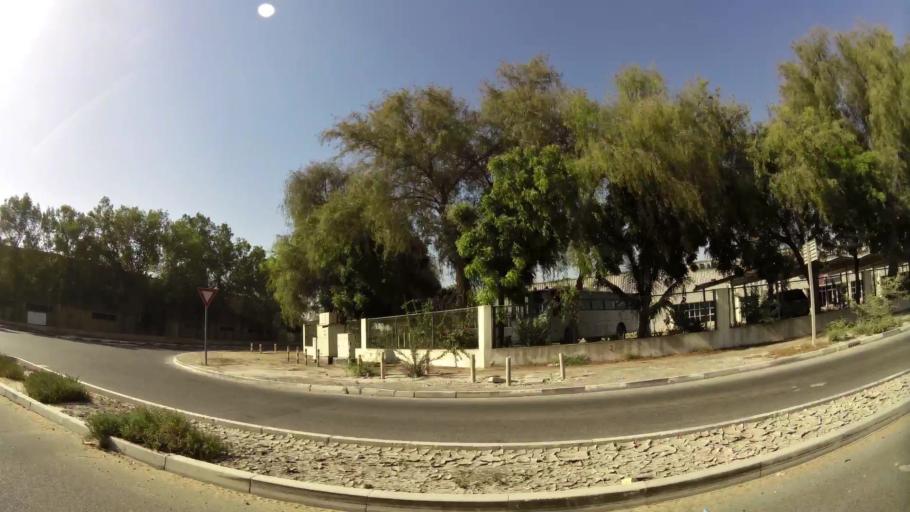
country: AE
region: Dubai
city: Dubai
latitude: 24.9931
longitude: 55.1039
